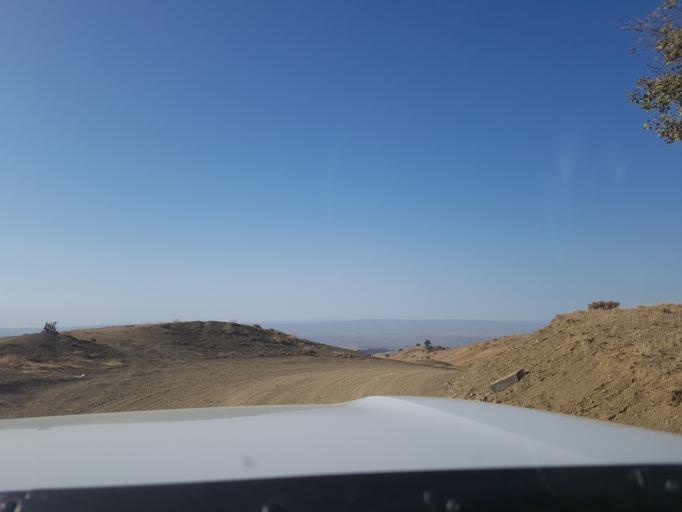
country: TM
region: Ahal
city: Baharly
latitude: 38.3440
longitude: 56.9031
